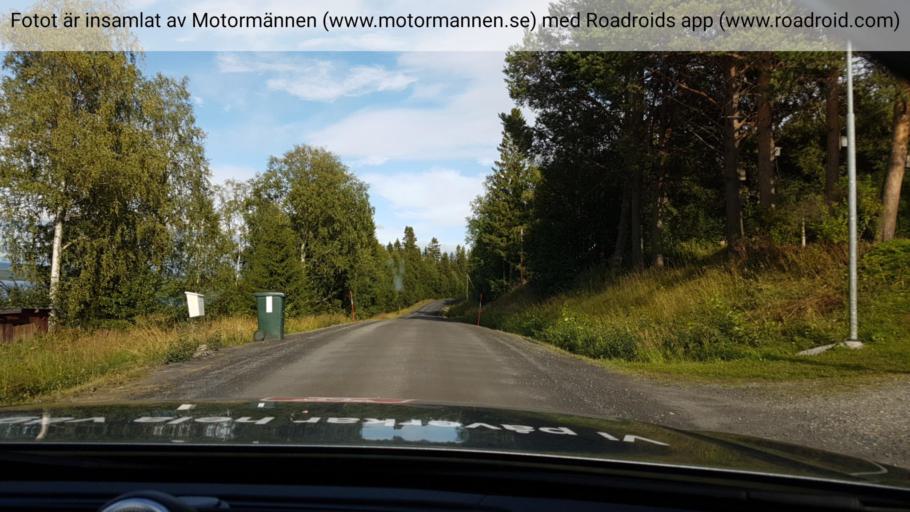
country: SE
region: Jaemtland
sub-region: Stroemsunds Kommun
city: Stroemsund
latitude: 64.1433
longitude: 15.6990
